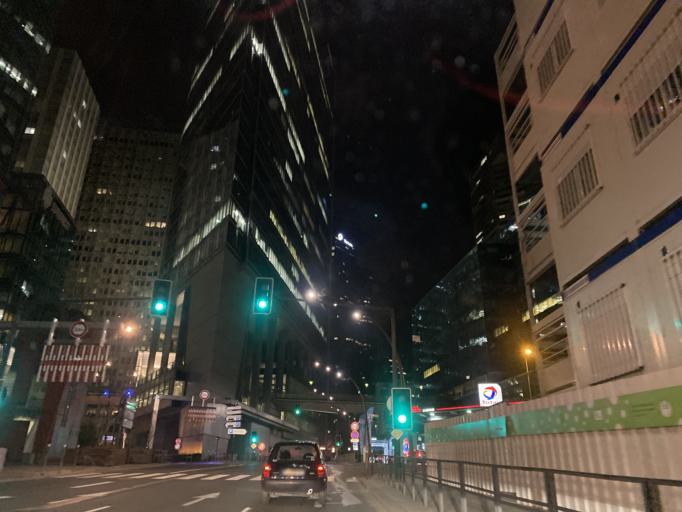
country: FR
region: Ile-de-France
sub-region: Departement des Hauts-de-Seine
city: La Defense
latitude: 48.8908
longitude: 2.2480
